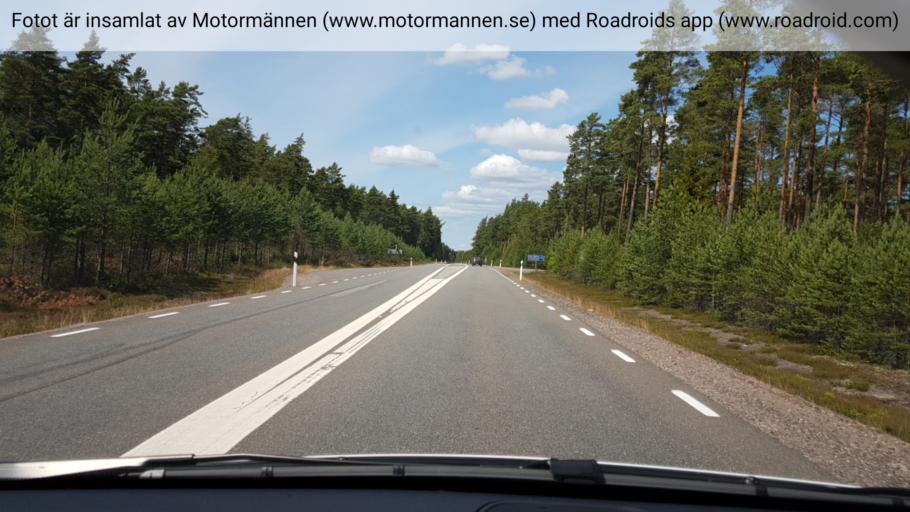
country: SE
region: Vaestra Goetaland
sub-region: Tibro Kommun
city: Tibro
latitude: 58.5537
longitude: 14.1328
